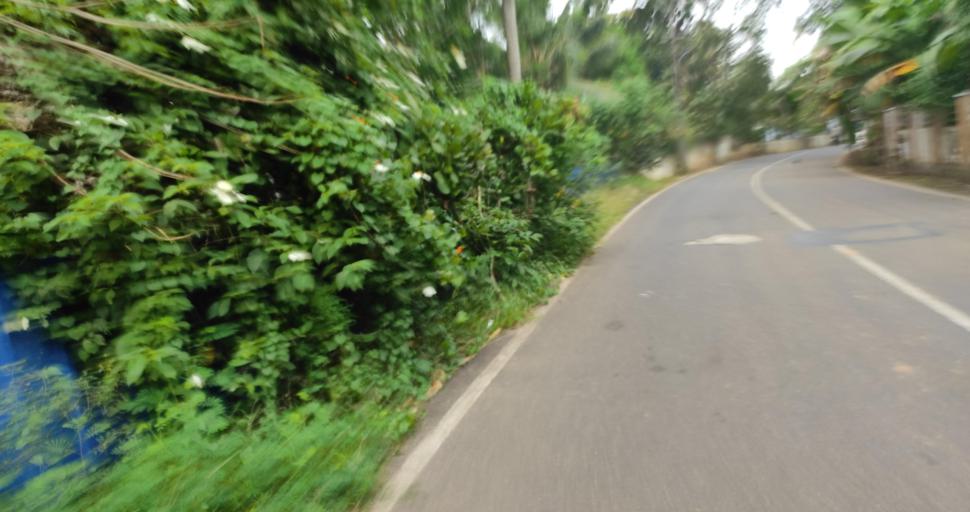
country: IN
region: Kerala
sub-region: Alappuzha
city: Shertallai
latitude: 9.6533
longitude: 76.3138
